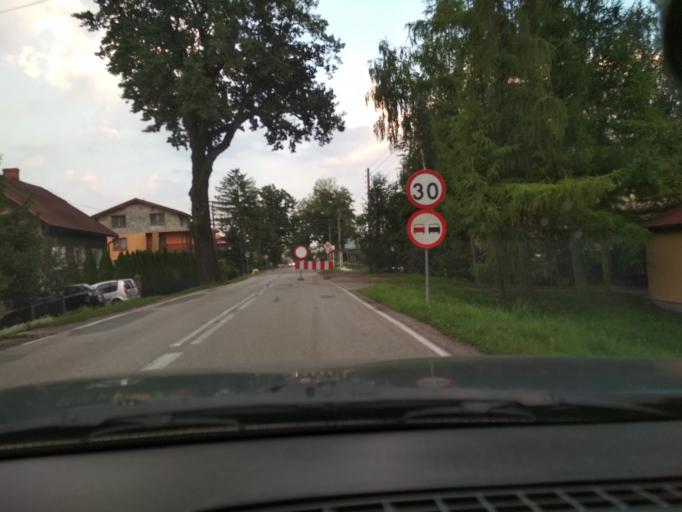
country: PL
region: Silesian Voivodeship
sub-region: Powiat cieszynski
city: Mnich
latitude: 49.8975
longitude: 18.7968
